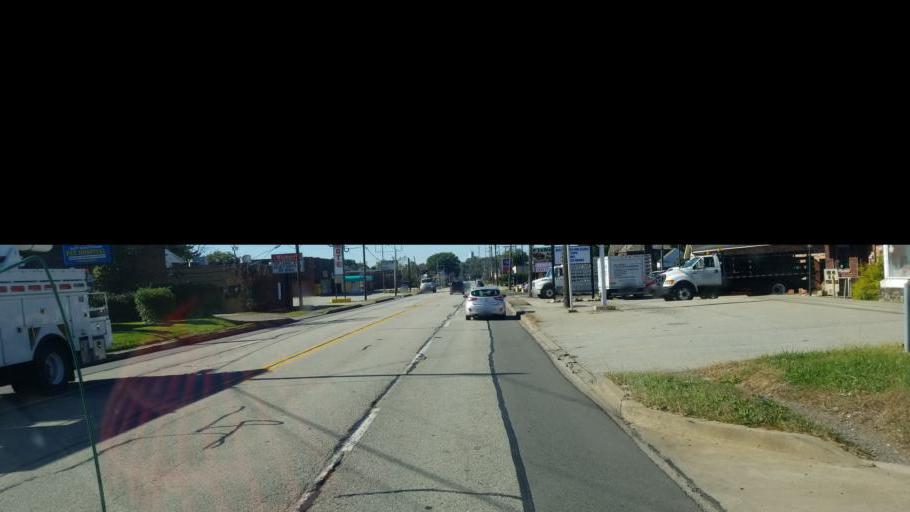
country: US
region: Pennsylvania
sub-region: Allegheny County
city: East McKeesport
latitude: 40.3777
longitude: -79.8024
